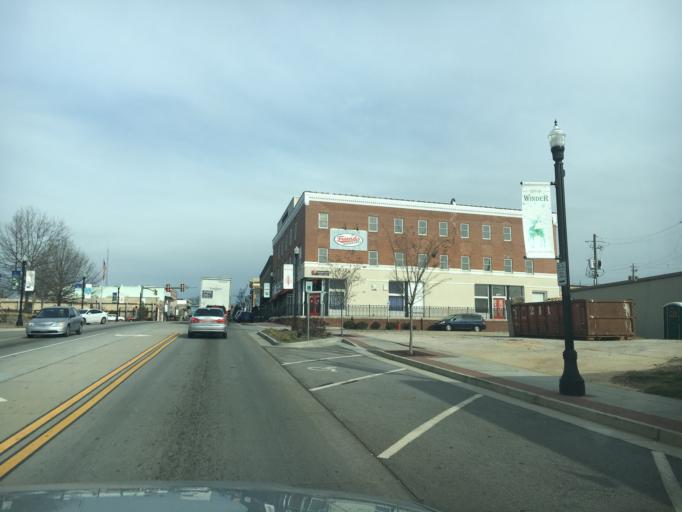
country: US
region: Georgia
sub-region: Barrow County
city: Winder
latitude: 33.9917
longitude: -83.7219
